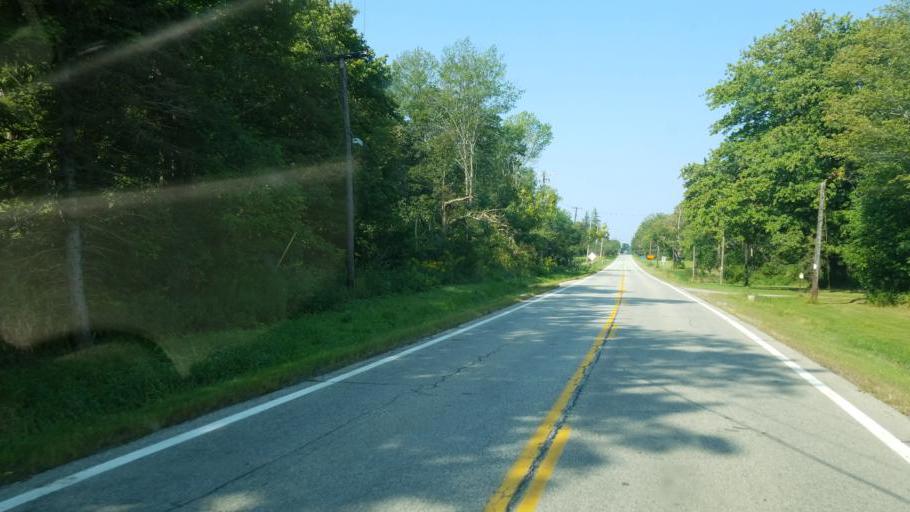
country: US
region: Ohio
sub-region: Geauga County
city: Chardon
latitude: 41.6072
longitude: -81.0031
